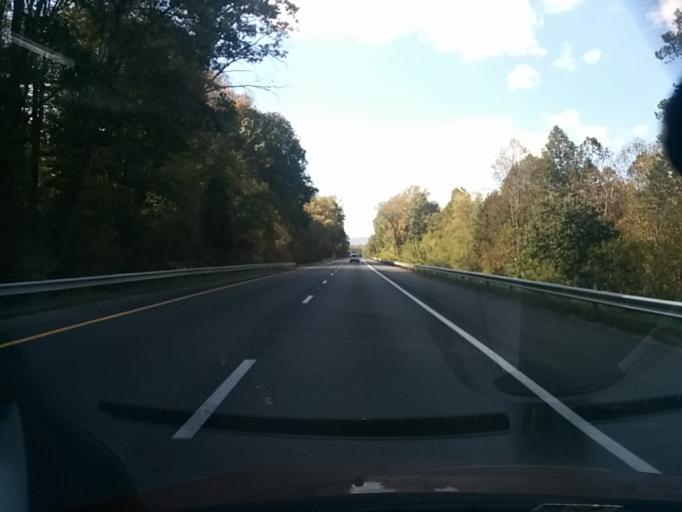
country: US
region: Virginia
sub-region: Albemarle County
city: Crozet
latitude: 38.0306
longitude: -78.6612
